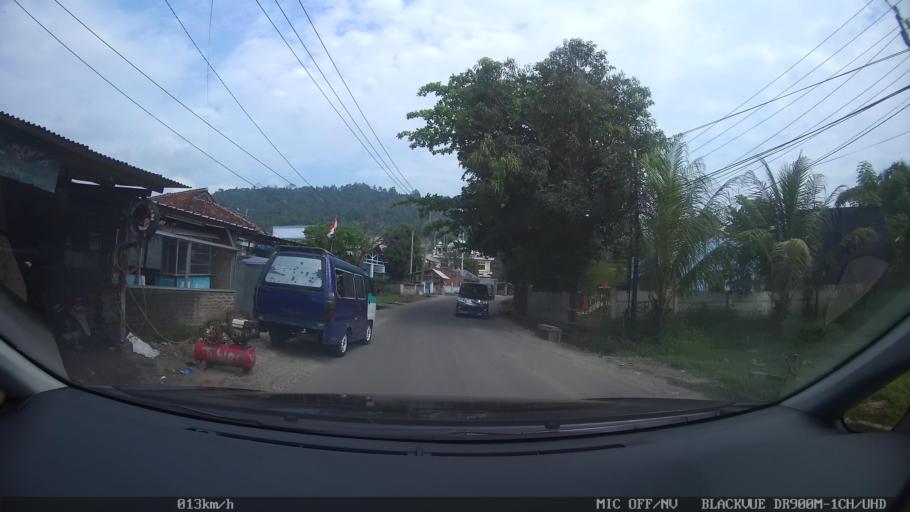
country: ID
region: Lampung
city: Bandarlampung
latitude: -5.4730
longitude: 105.2449
